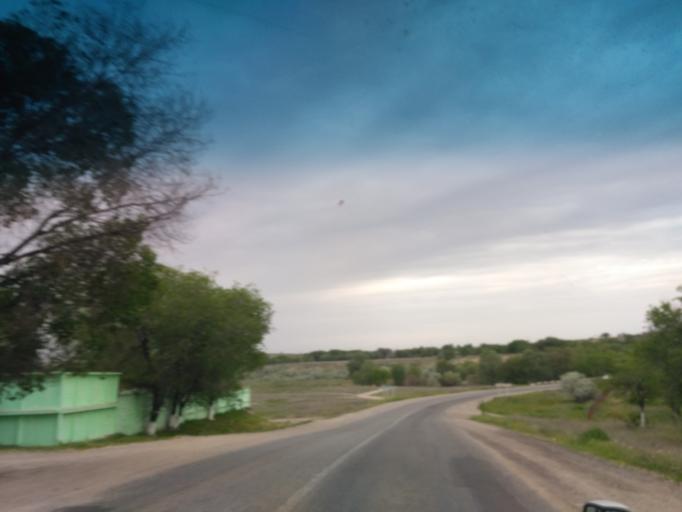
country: KZ
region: Almaty Oblysy
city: Burunday
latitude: 43.4613
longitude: 76.7217
